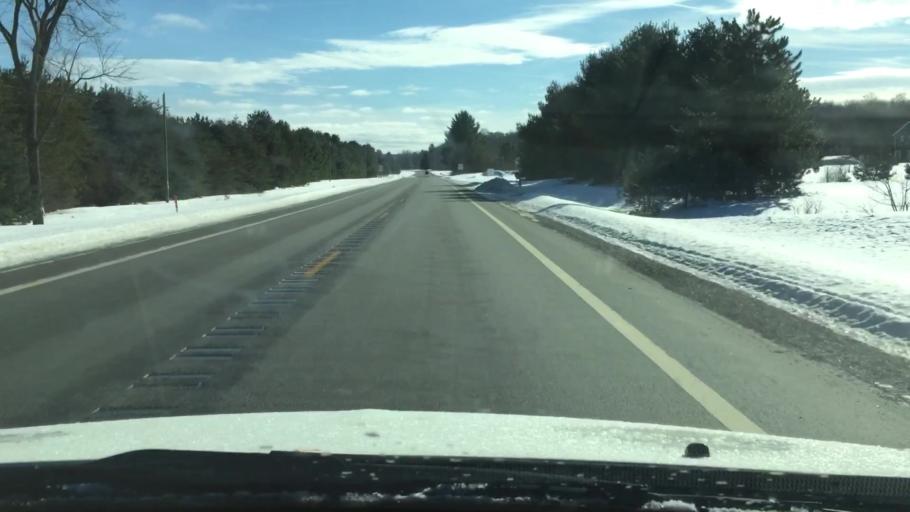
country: US
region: Michigan
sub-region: Charlevoix County
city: East Jordan
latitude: 45.0748
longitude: -85.0872
